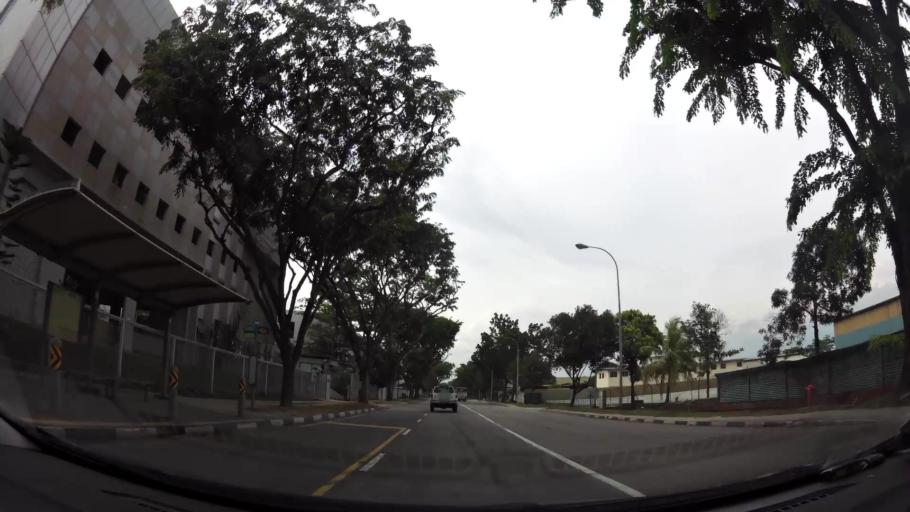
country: MY
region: Johor
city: Johor Bahru
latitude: 1.4357
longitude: 103.7486
